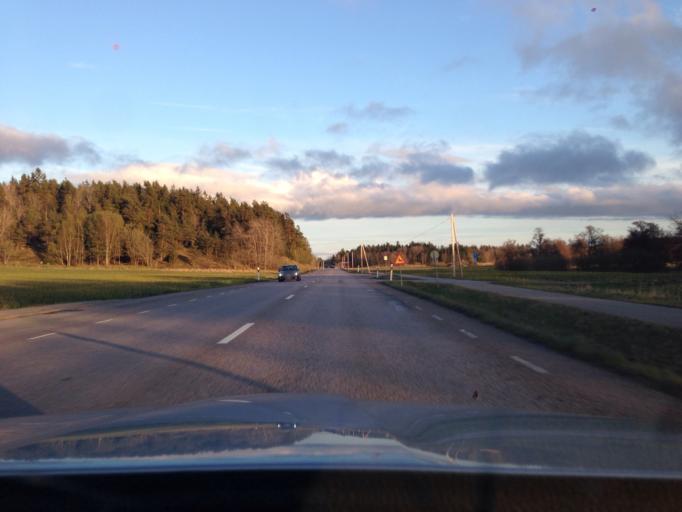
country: SE
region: Soedermanland
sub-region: Trosa Kommun
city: Trosa
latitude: 58.9207
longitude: 17.5415
